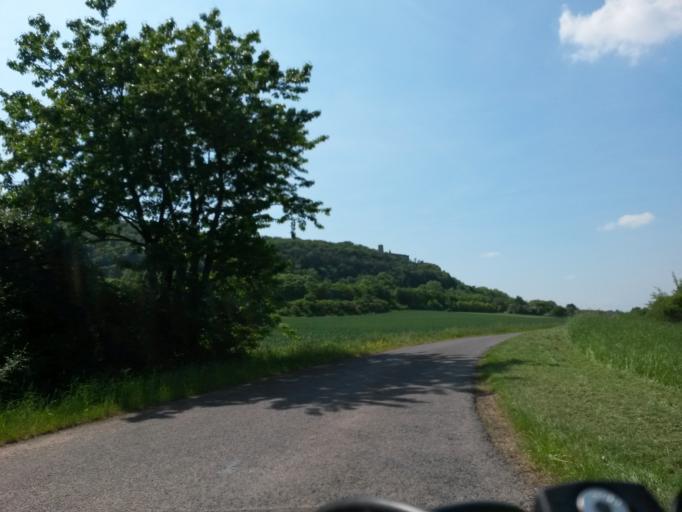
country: DE
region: Bavaria
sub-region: Regierungsbezirk Unterfranken
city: Elfershausen
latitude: 50.1409
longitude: 9.9860
